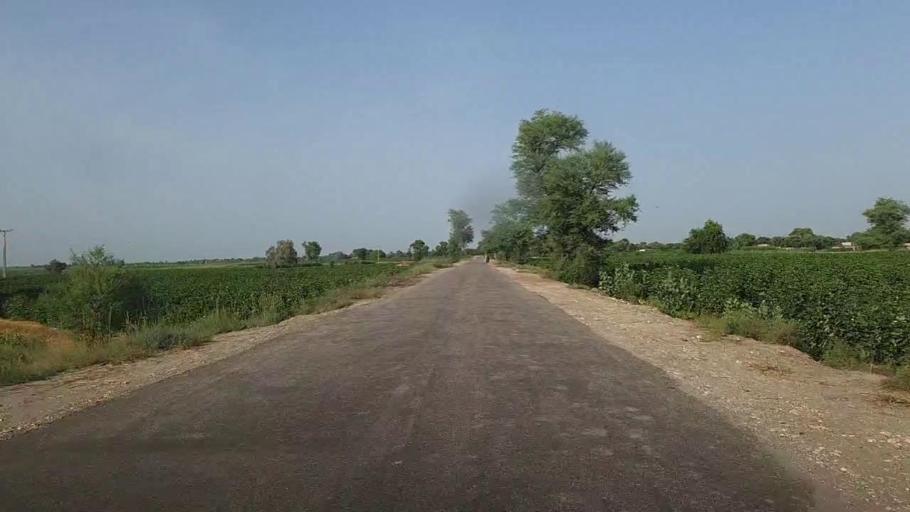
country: PK
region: Sindh
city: Khairpur
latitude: 28.0772
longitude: 69.8309
